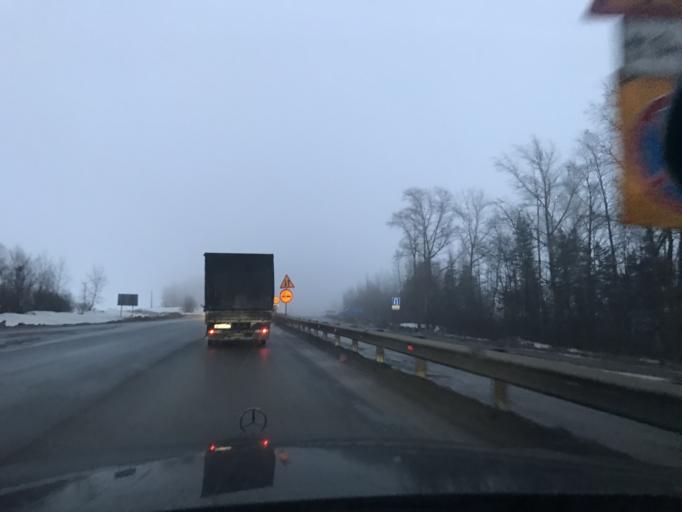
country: RU
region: Vladimir
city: Novovyazniki
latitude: 56.2153
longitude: 42.2520
